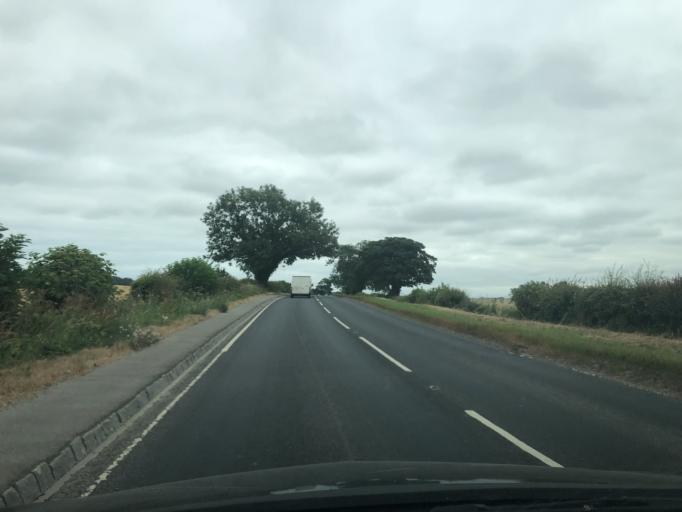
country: GB
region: England
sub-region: North Yorkshire
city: East Ayton
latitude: 54.2503
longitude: -0.4711
